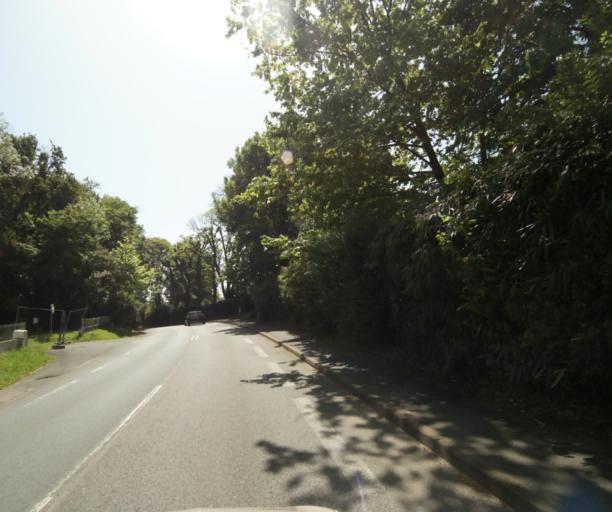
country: FR
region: Aquitaine
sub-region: Departement des Pyrenees-Atlantiques
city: Bayonne
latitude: 43.4763
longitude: -1.4568
